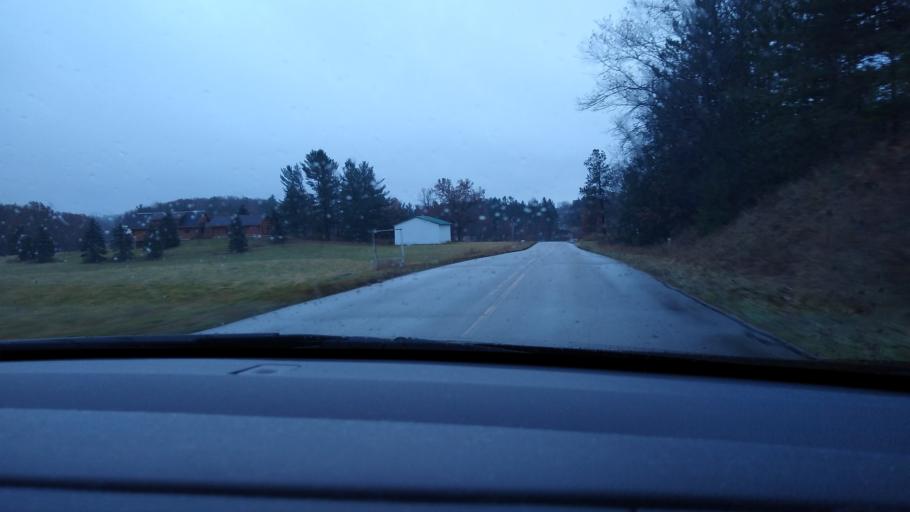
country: US
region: Michigan
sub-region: Wexford County
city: Cadillac
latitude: 44.1887
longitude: -85.3955
